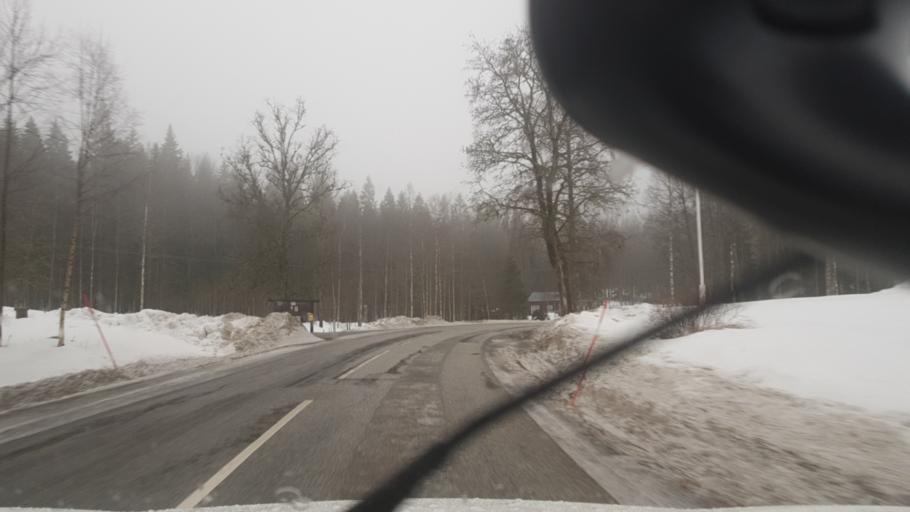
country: SE
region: Vaermland
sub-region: Eda Kommun
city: Amotfors
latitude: 59.5785
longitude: 12.2556
